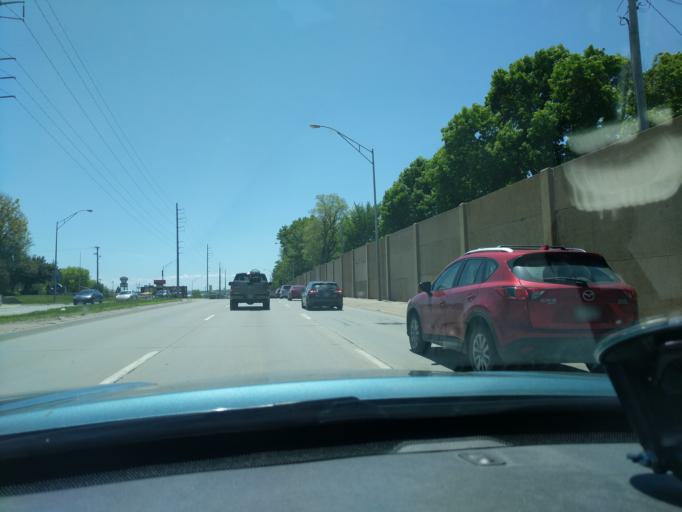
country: US
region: Nebraska
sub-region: Douglas County
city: Ralston
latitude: 41.2301
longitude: -96.0239
